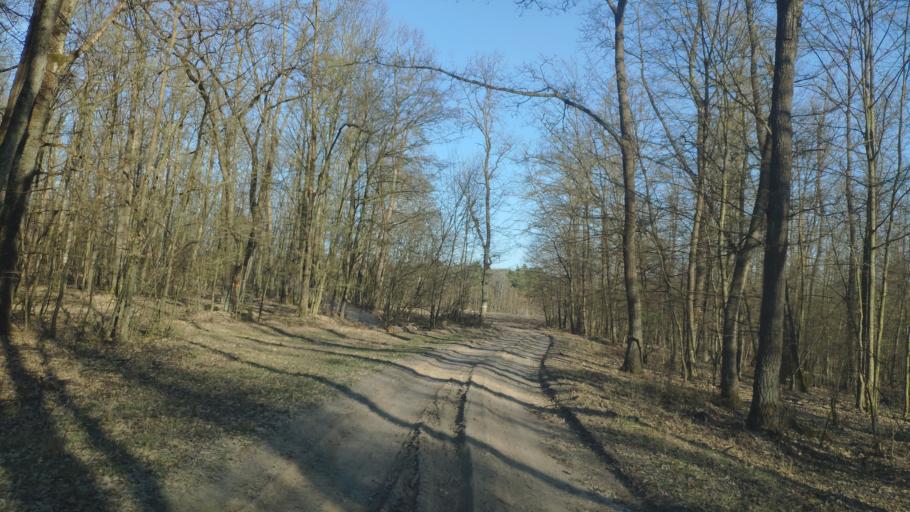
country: HU
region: Borsod-Abauj-Zemplen
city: Putnok
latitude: 48.5012
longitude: 20.2990
